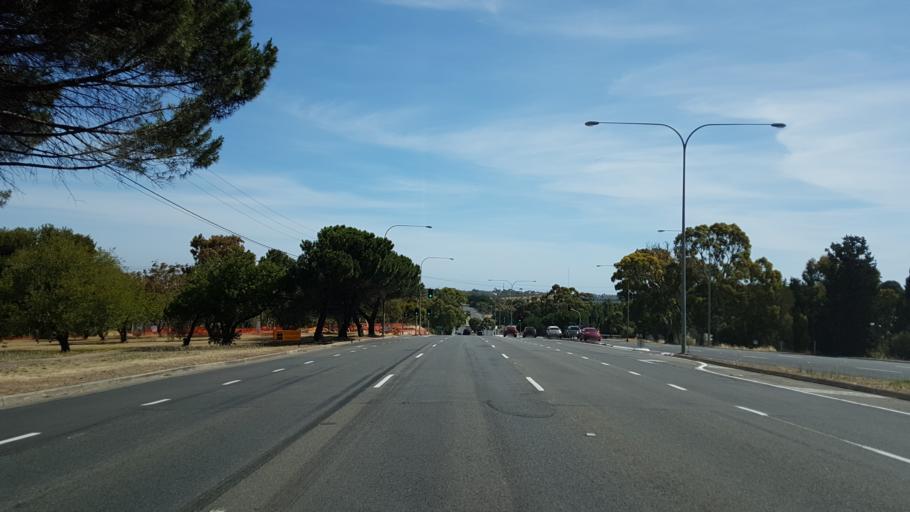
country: AU
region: South Australia
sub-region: Marion
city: Trott Park
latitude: -35.0746
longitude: 138.5513
